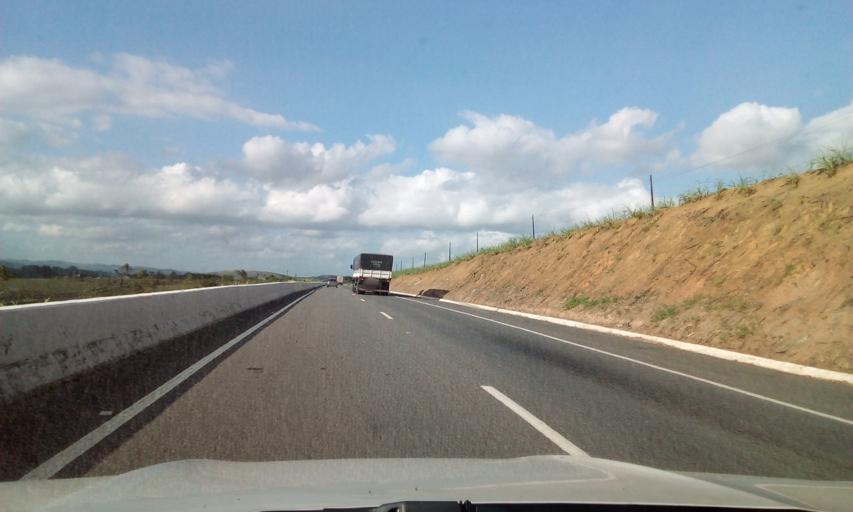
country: BR
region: Pernambuco
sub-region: Ribeirao
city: Ribeirao
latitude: -8.4783
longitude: -35.3717
